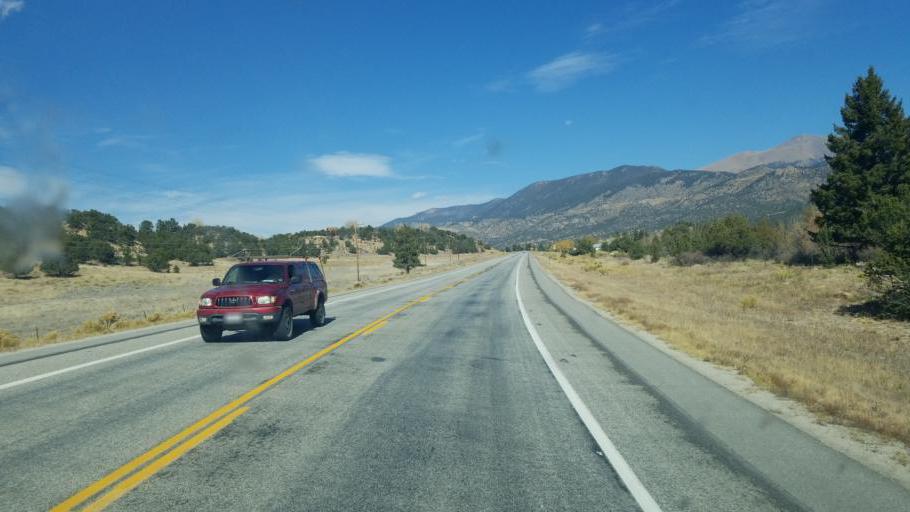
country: US
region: Colorado
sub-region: Chaffee County
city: Buena Vista
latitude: 38.8951
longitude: -106.1737
